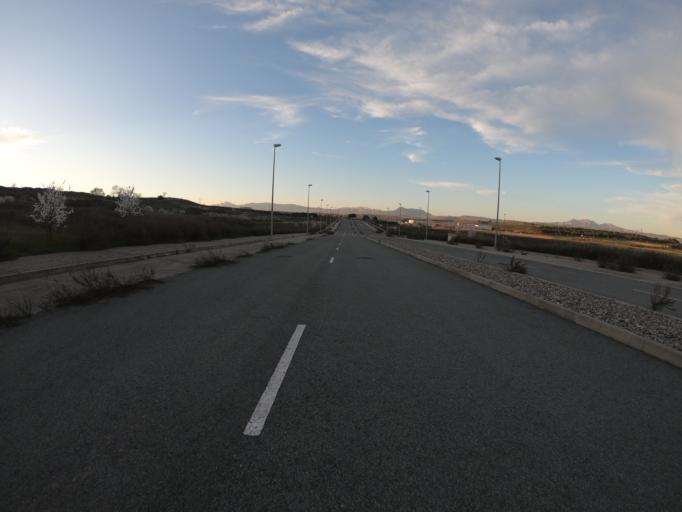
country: ES
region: Basque Country
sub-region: Provincia de Alava
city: Oyon
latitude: 42.4835
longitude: -2.4144
